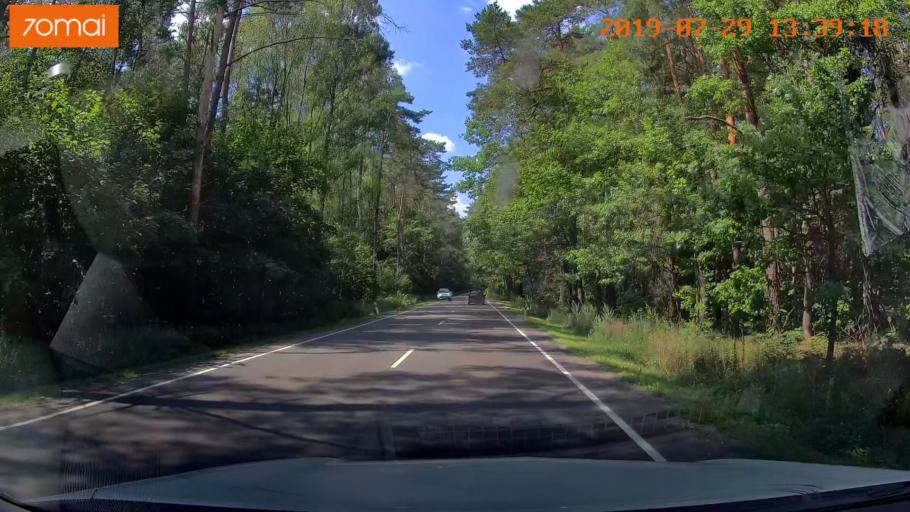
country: RU
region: Kaliningrad
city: Svetlyy
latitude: 54.7236
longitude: 20.1555
